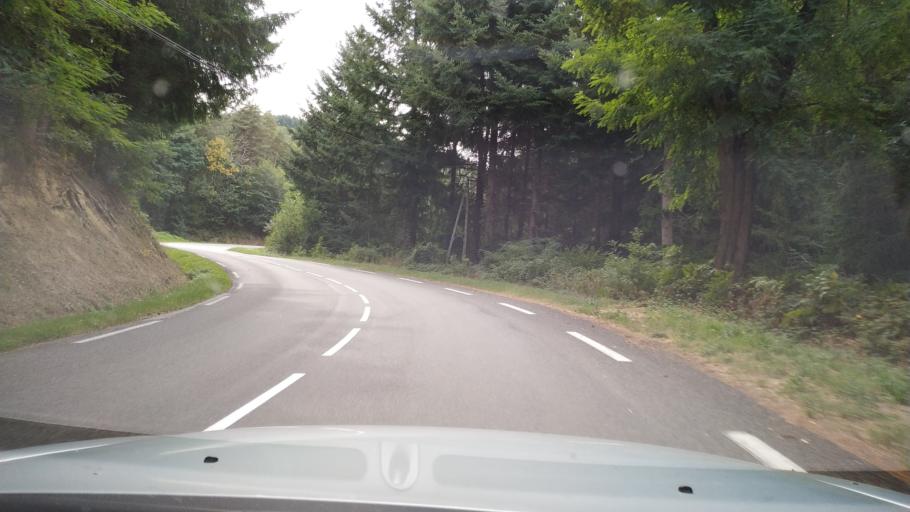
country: FR
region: Rhone-Alpes
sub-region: Departement de l'Ardeche
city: Desaignes
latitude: 45.0001
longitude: 4.5031
